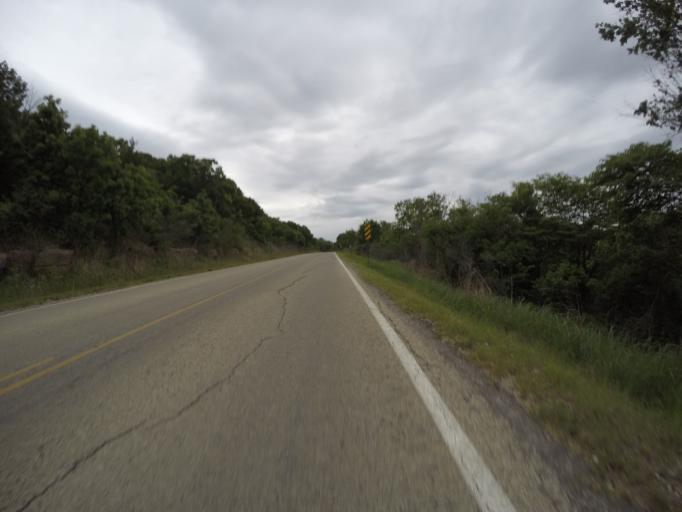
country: US
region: Kansas
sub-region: Pottawatomie County
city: Wamego
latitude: 39.1839
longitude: -96.4058
